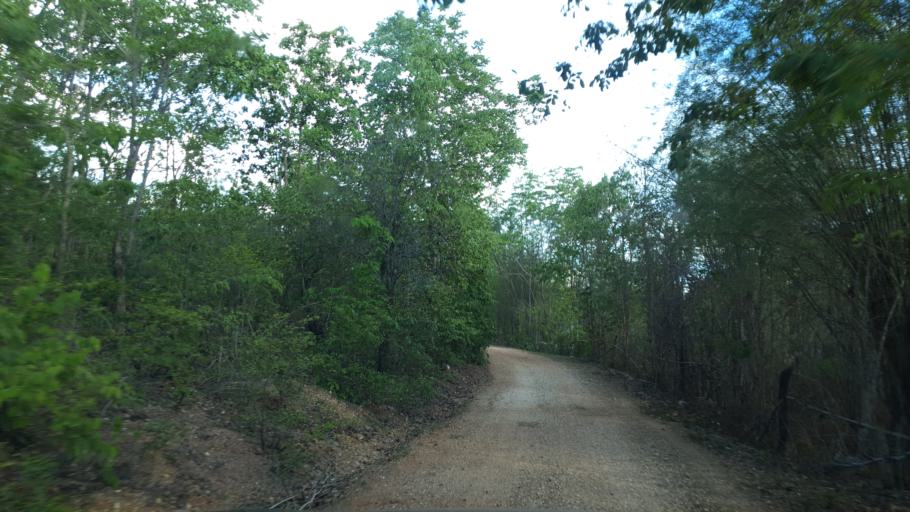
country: TH
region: Lampang
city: Sop Prap
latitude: 17.8846
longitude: 99.2923
